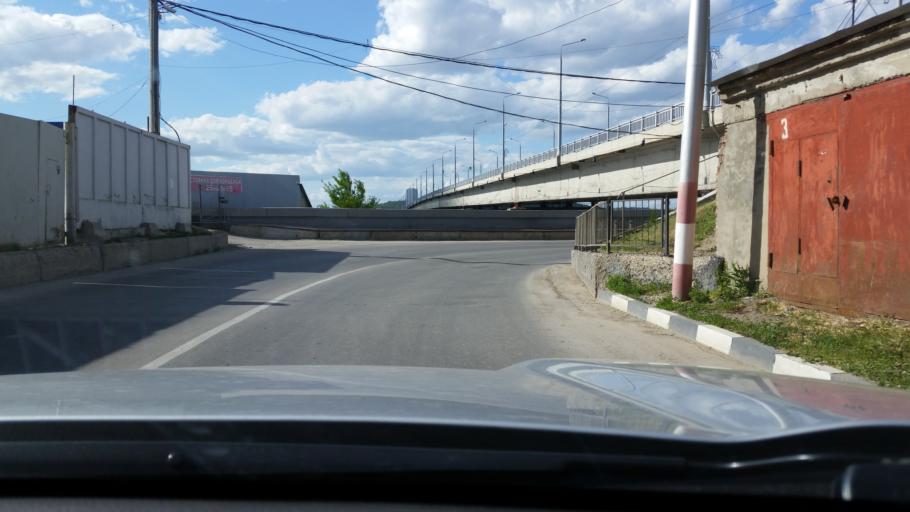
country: RU
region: Saratov
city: Engel's
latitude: 51.5055
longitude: 46.0778
